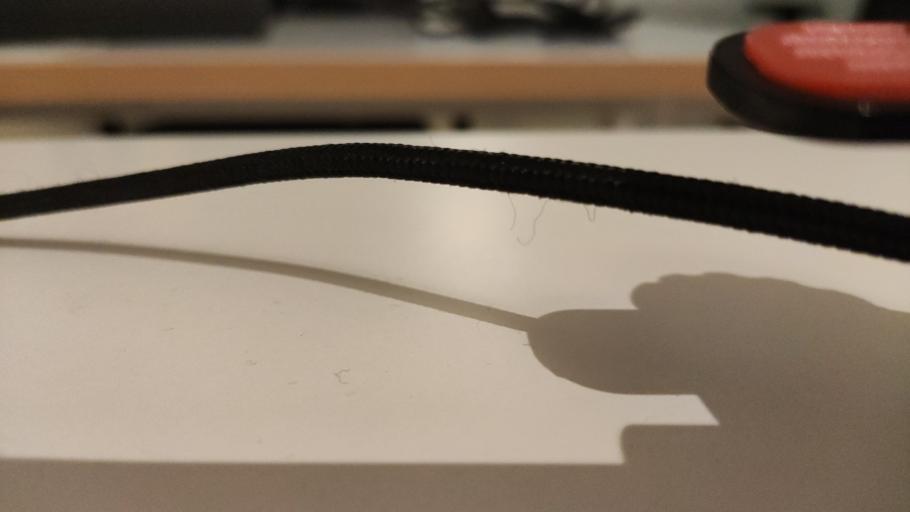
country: RU
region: Moskovskaya
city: Malino
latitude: 55.1081
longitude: 38.1139
